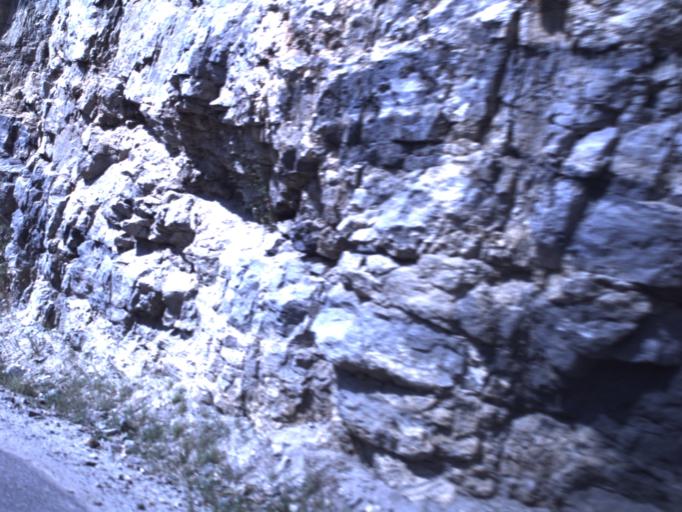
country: US
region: Idaho
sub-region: Bear Lake County
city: Paris
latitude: 41.9591
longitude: -111.5088
